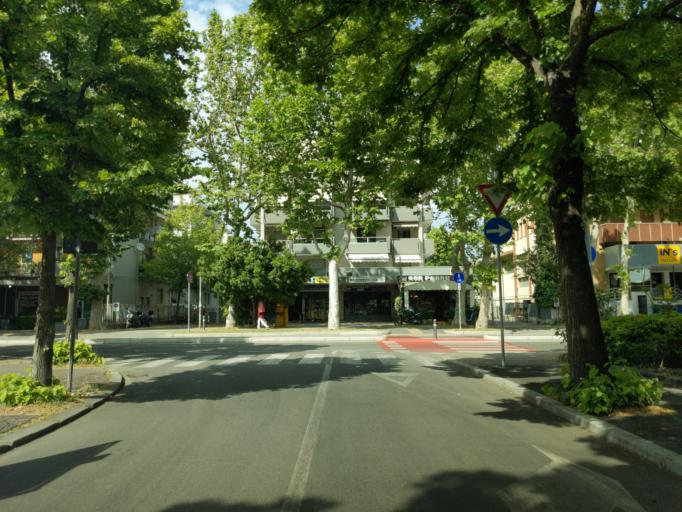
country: IT
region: Emilia-Romagna
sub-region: Provincia di Rimini
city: Rimini
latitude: 44.0467
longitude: 12.5818
